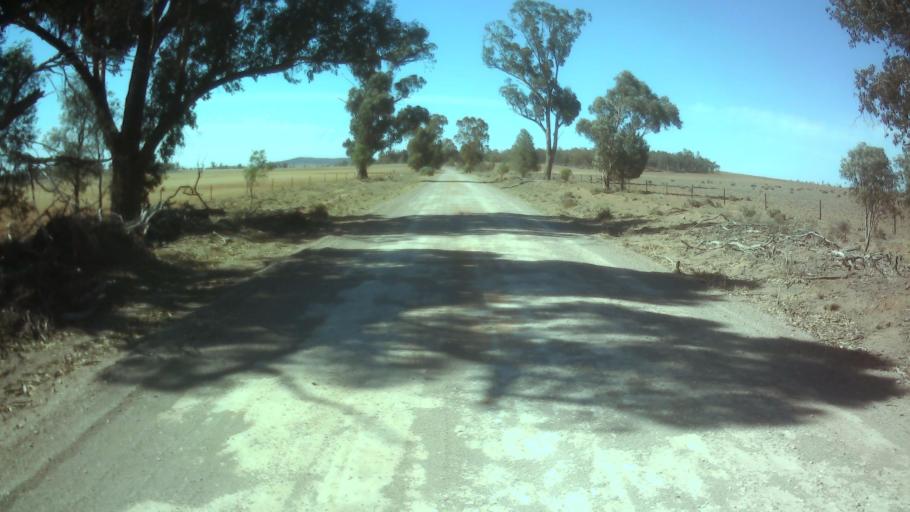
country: AU
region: New South Wales
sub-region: Forbes
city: Forbes
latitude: -33.7199
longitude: 147.7458
